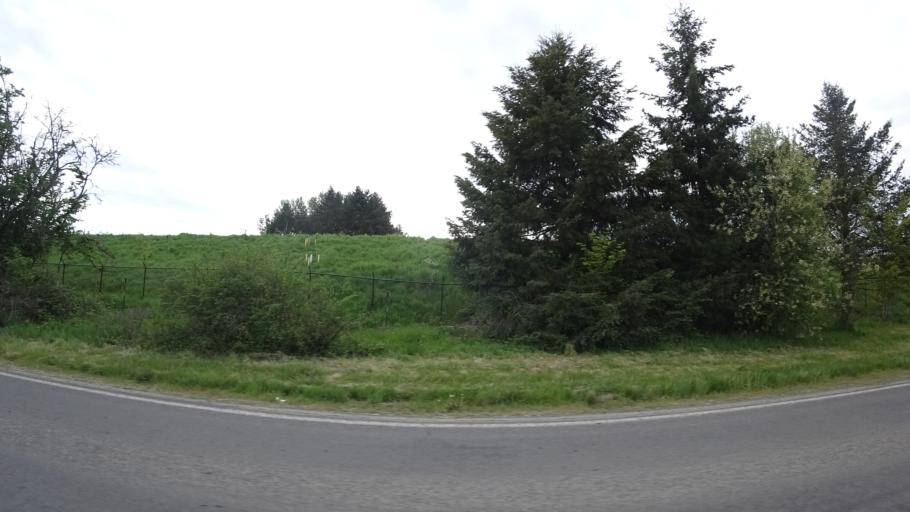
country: US
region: Oregon
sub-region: Washington County
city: Hillsboro
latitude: 45.4897
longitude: -122.9701
